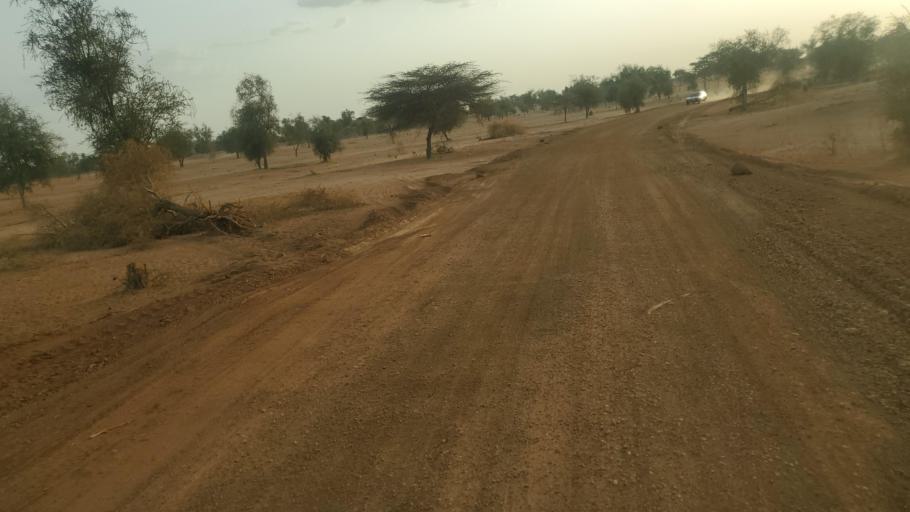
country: SN
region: Louga
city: Dara
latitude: 15.3778
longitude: -15.5986
